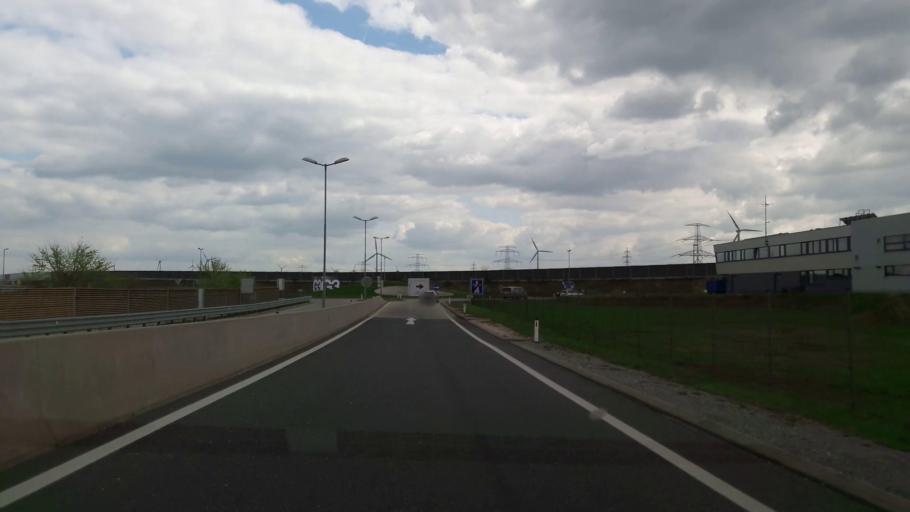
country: AT
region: Lower Austria
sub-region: Politischer Bezirk Mistelbach
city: Grossebersdorf
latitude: 48.3490
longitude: 16.4736
